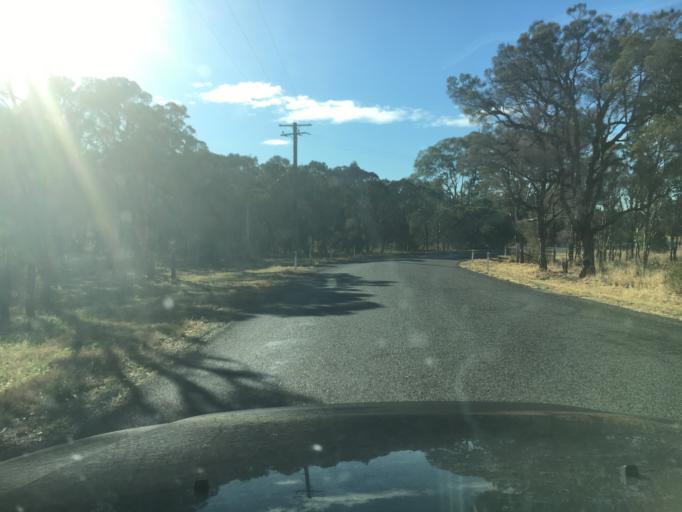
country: AU
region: New South Wales
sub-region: Singleton
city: Singleton
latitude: -32.5405
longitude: 151.2403
